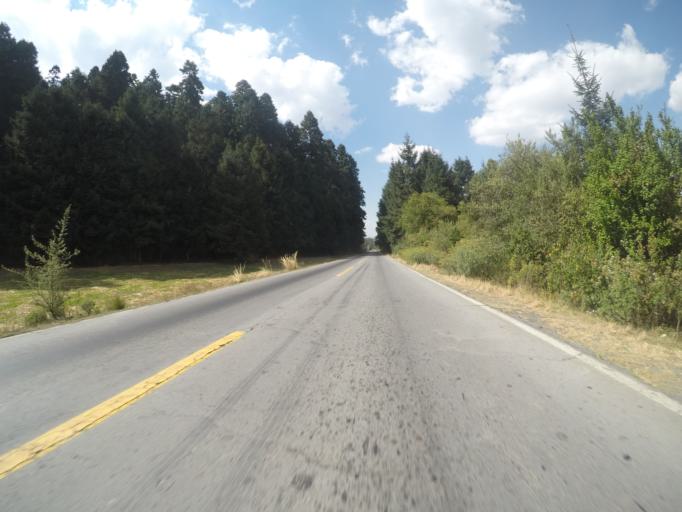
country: MX
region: Mexico
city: Cerro La Calera
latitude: 19.1922
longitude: -99.8082
